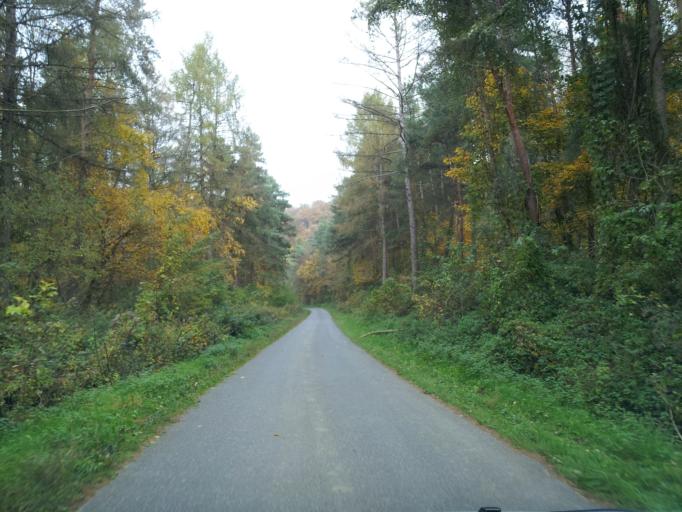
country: HU
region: Gyor-Moson-Sopron
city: Pannonhalma
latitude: 47.4825
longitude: 17.7140
